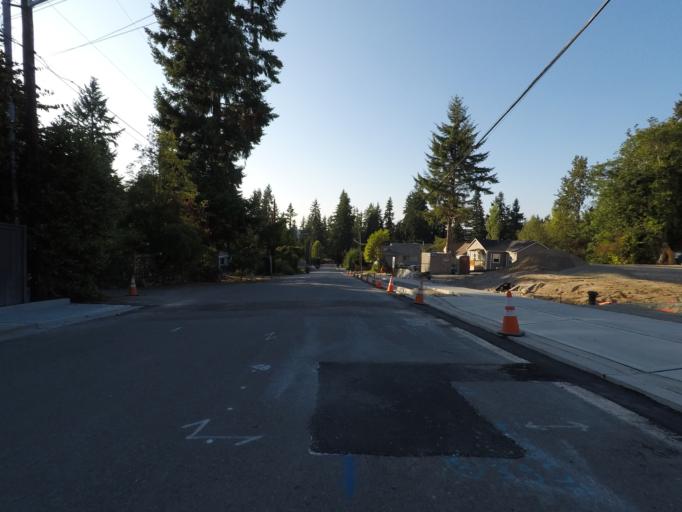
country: US
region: Washington
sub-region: King County
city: Kenmore
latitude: 47.7459
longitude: -122.2345
